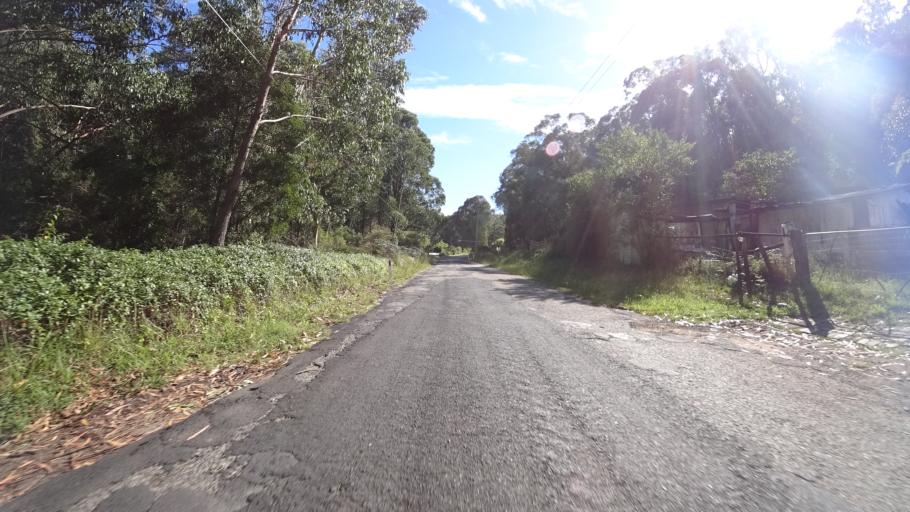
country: AU
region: New South Wales
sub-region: Lithgow
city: Lithgow
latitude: -33.4572
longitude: 150.1719
